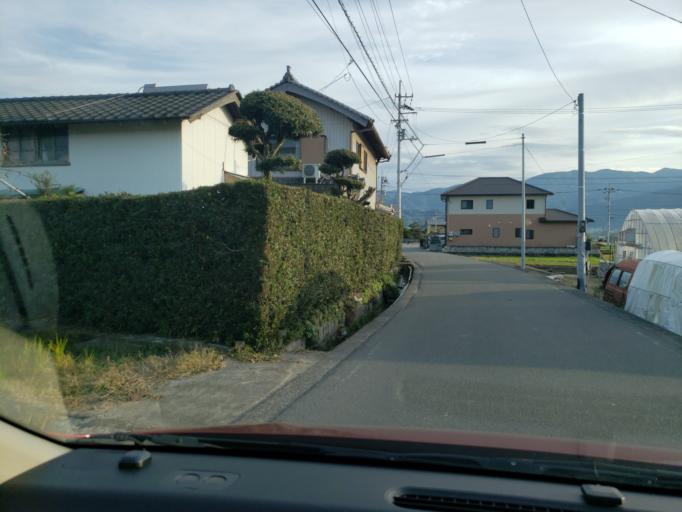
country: JP
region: Tokushima
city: Wakimachi
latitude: 34.0834
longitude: 134.2271
